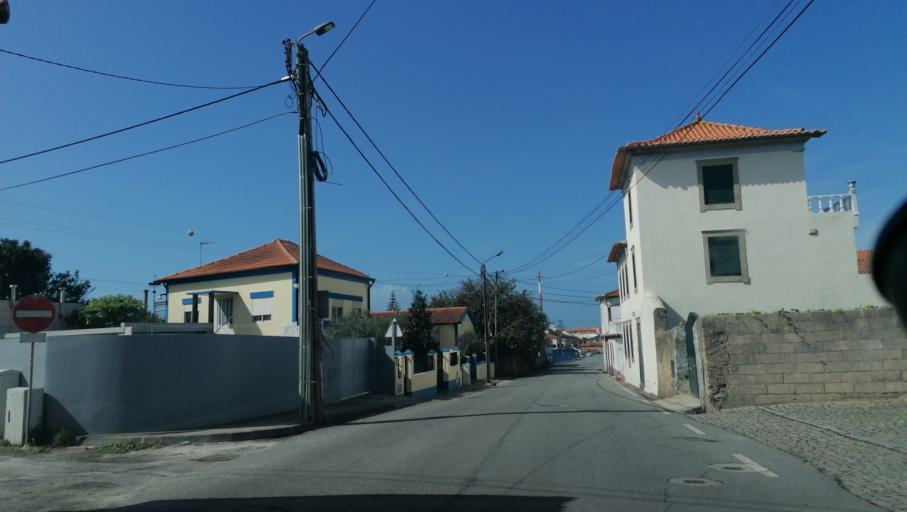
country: PT
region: Aveiro
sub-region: Espinho
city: Silvalde
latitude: 40.9987
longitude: -8.6173
